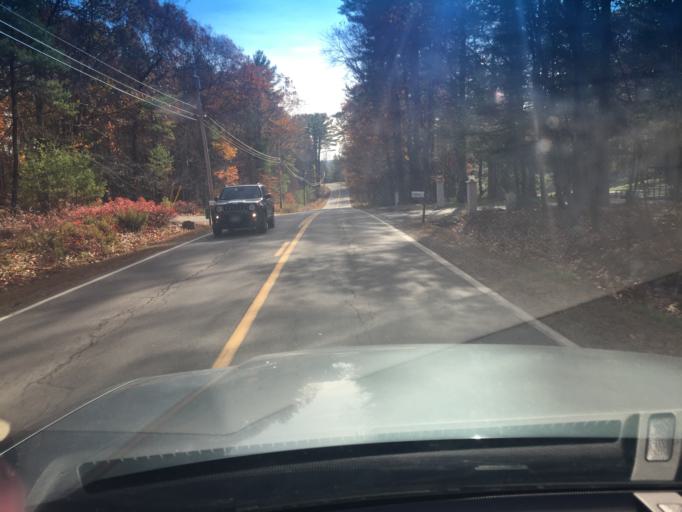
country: US
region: Maine
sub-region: York County
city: Eliot
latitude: 43.1882
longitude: -70.7467
